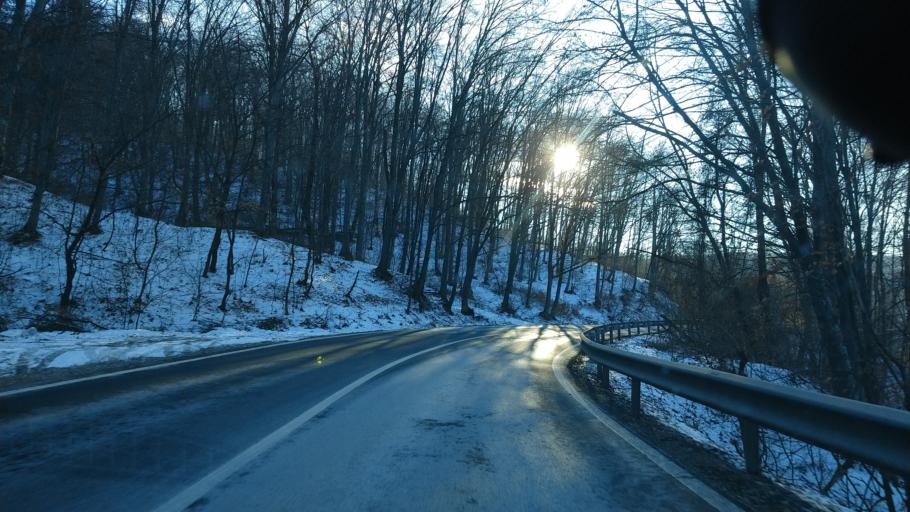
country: RO
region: Bacau
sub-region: Comuna Luizi-Calugara
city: Luizi-Calugara
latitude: 46.5509
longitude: 26.8202
